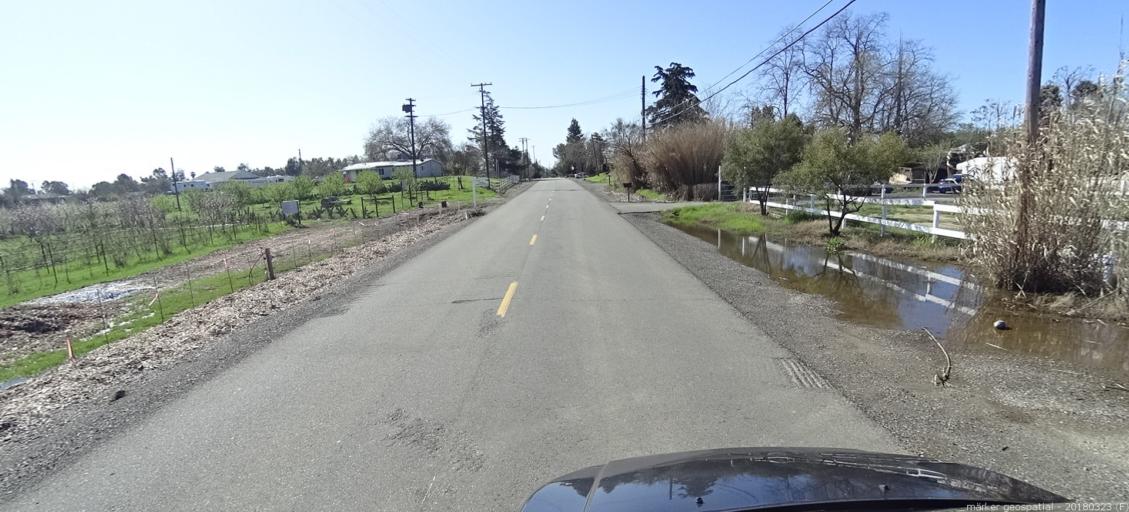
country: US
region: California
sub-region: Sacramento County
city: Elverta
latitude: 38.6974
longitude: -121.4747
